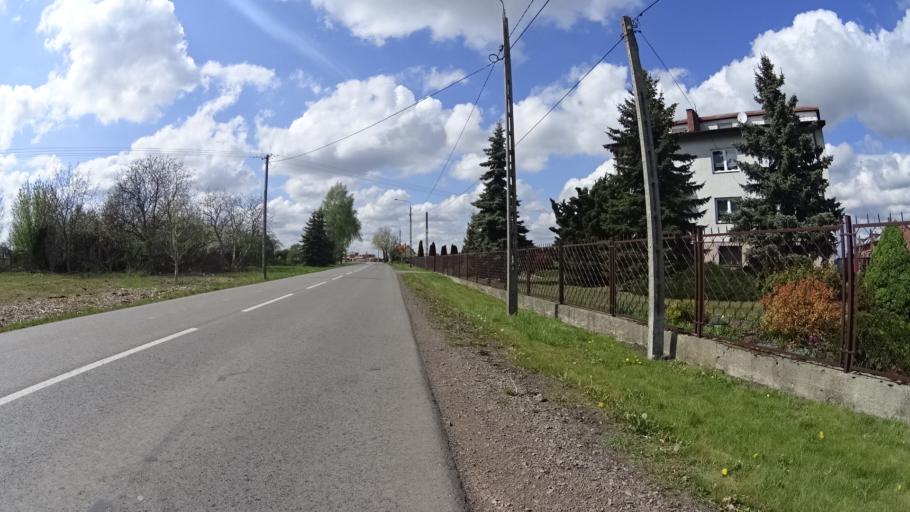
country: PL
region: Masovian Voivodeship
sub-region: Powiat warszawski zachodni
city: Jozefow
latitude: 52.2330
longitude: 20.7319
